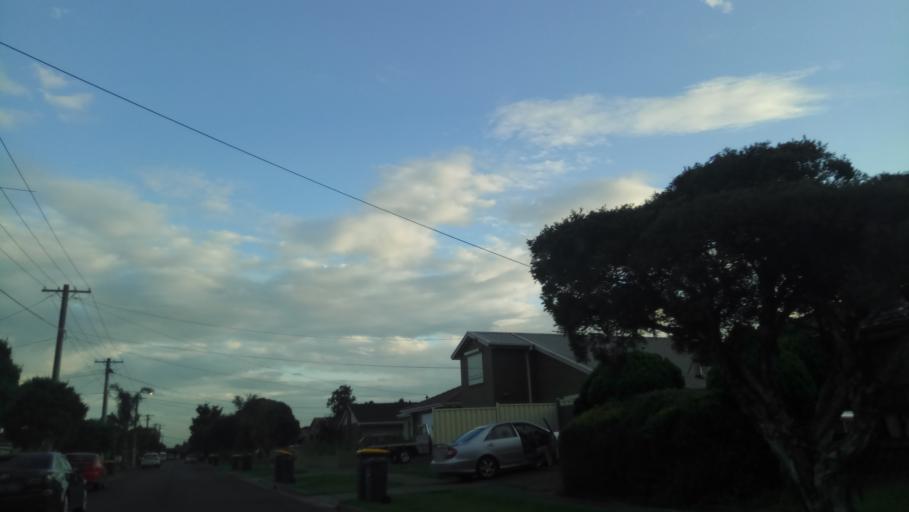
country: AU
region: Victoria
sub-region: Hobsons Bay
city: Altona Meadows
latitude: -37.8887
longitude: 144.7805
